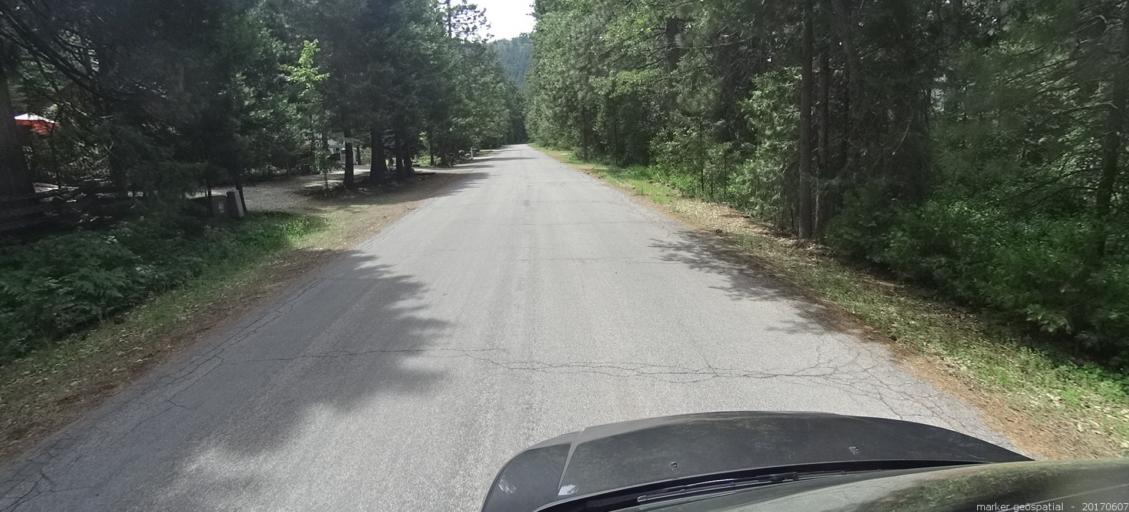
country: US
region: California
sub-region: Siskiyou County
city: Mount Shasta
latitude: 41.3319
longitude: -122.3579
